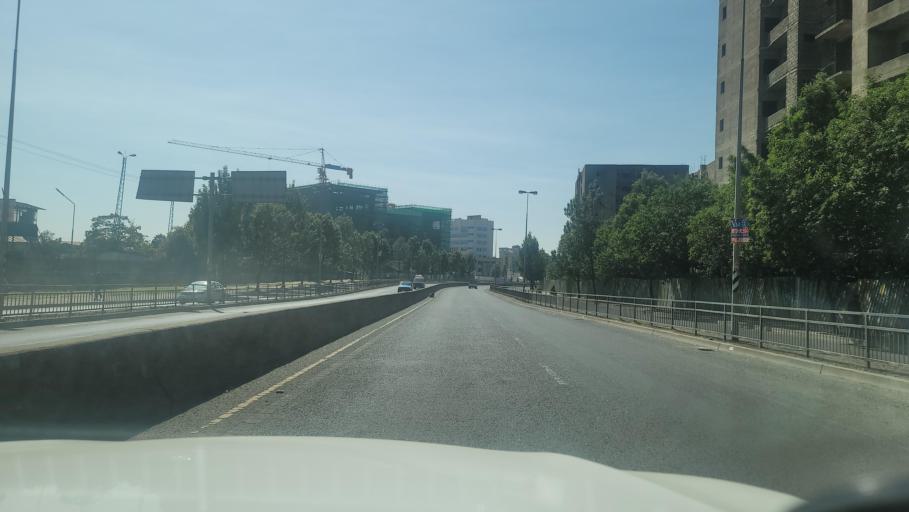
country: ET
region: Adis Abeba
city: Addis Ababa
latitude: 9.0138
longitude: 38.8036
